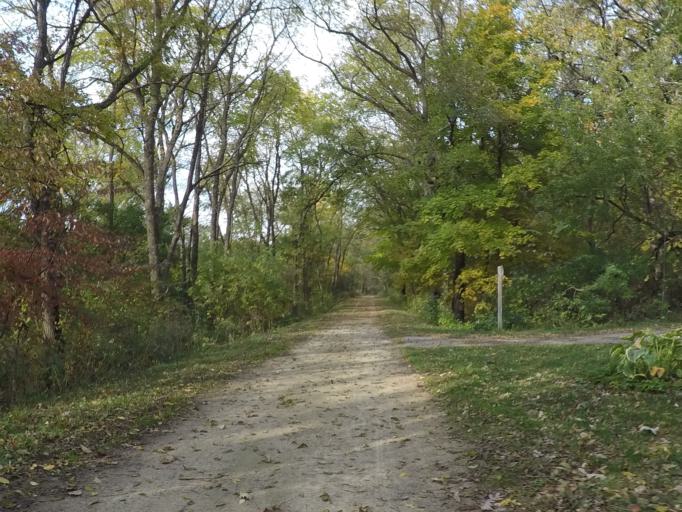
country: US
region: Wisconsin
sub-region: Dane County
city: Mount Horeb
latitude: 43.0146
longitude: -89.8106
